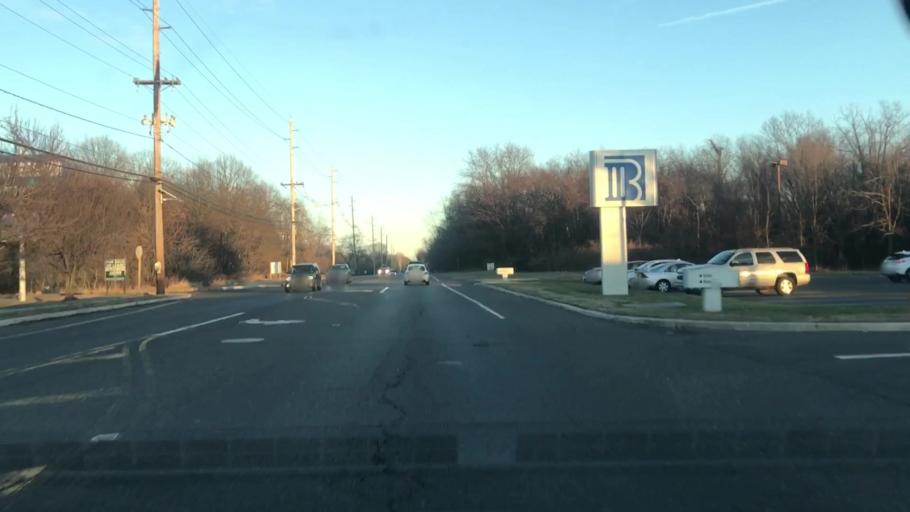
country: US
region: New Jersey
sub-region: Burlington County
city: Willingboro
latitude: 40.0497
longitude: -74.8701
